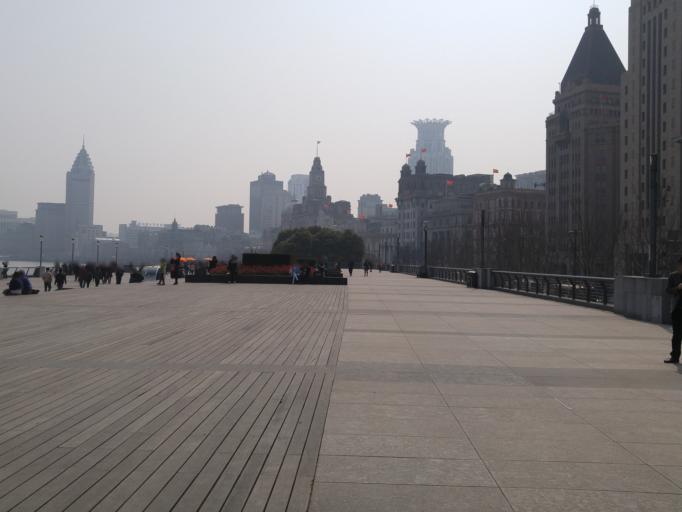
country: CN
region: Shanghai Shi
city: Hongkou
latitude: 31.2426
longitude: 121.4862
